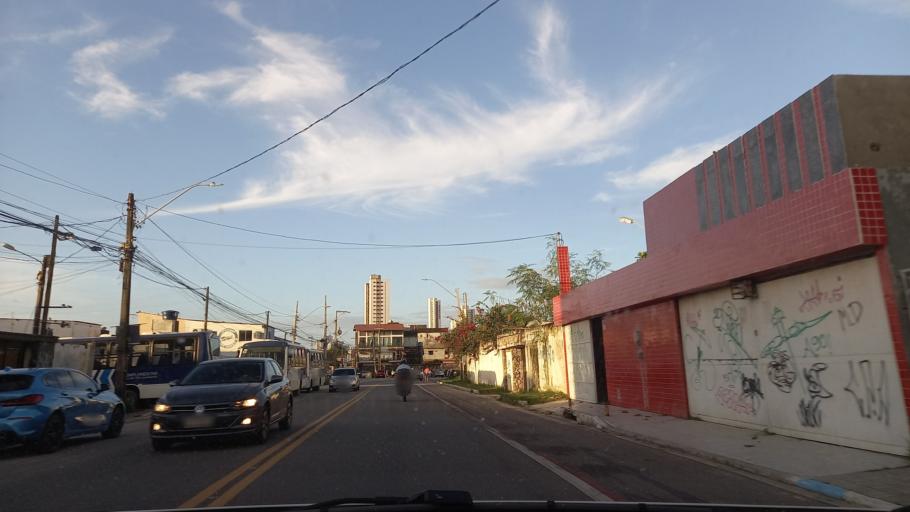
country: BR
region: Pernambuco
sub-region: Jaboatao Dos Guararapes
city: Jaboatao
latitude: -8.2211
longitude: -34.9268
